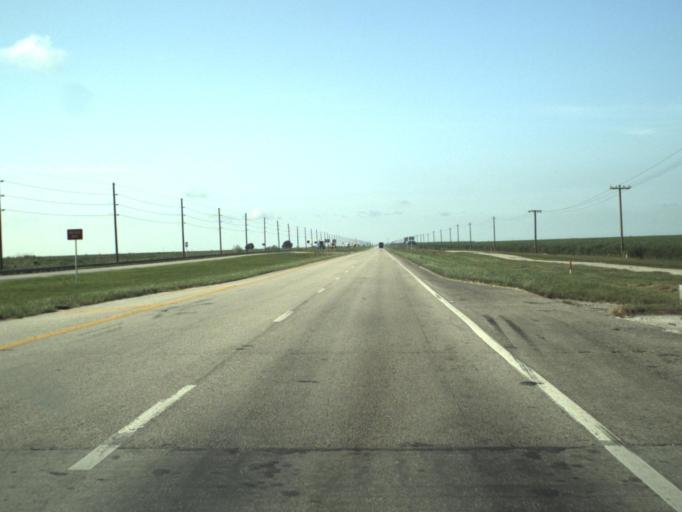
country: US
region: Florida
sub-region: Palm Beach County
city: South Bay
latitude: 26.6096
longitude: -80.7118
